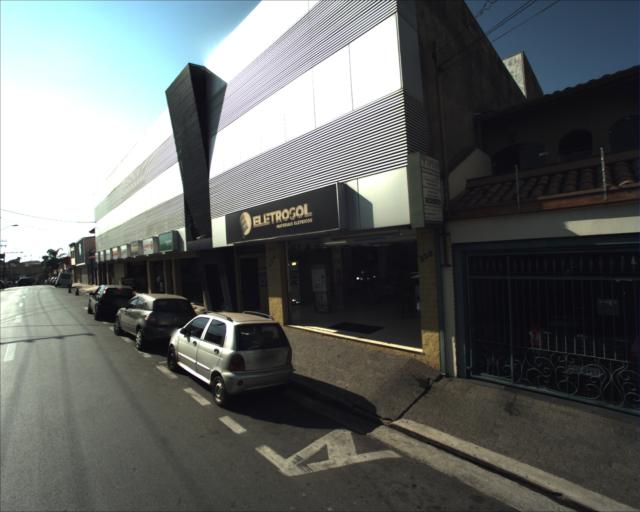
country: BR
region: Sao Paulo
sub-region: Sorocaba
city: Sorocaba
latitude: -23.4937
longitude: -47.4572
